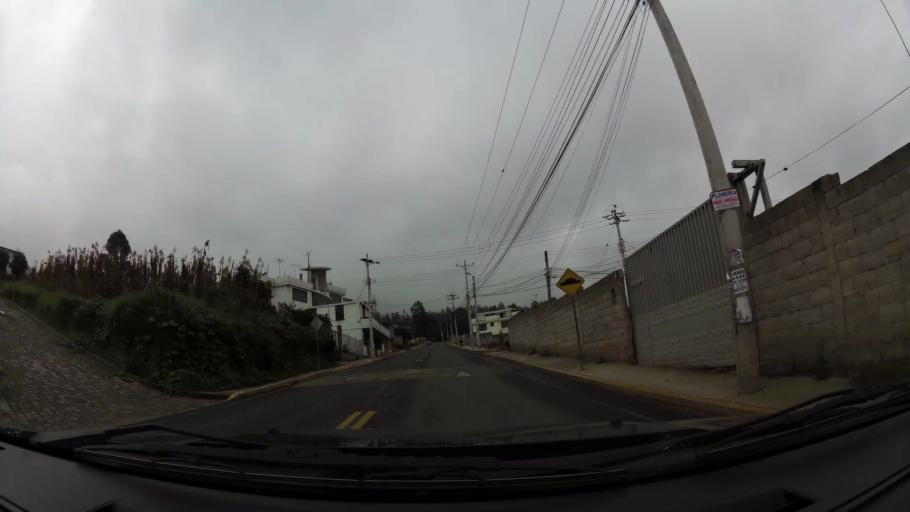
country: EC
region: Pichincha
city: Quito
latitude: -0.2645
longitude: -78.4807
